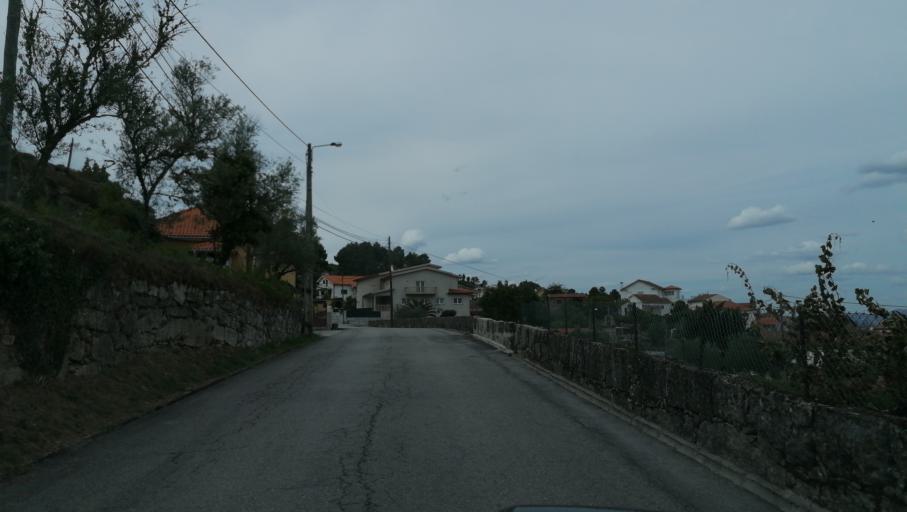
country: PT
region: Vila Real
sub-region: Vila Pouca de Aguiar
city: Vila Pouca de Aguiar
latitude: 41.5476
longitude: -7.6178
